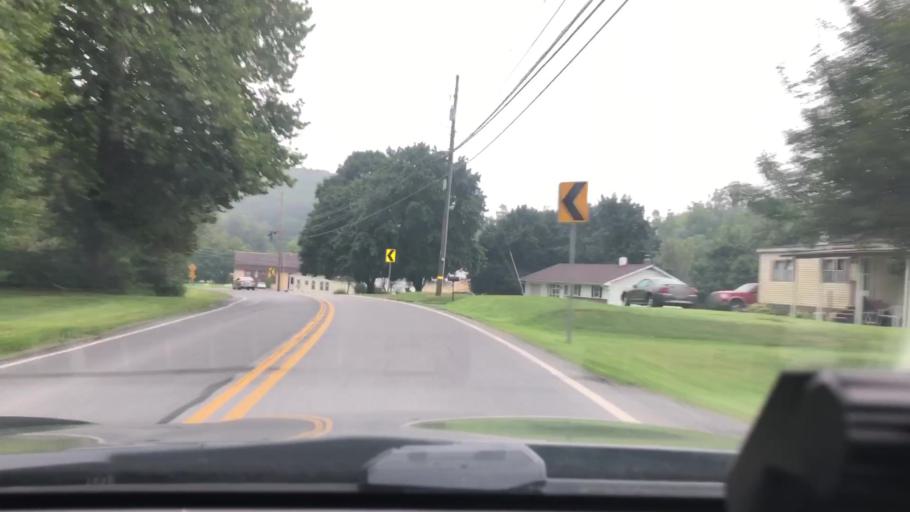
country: US
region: Pennsylvania
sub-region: Berks County
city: Kutztown
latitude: 40.5336
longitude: -75.7860
